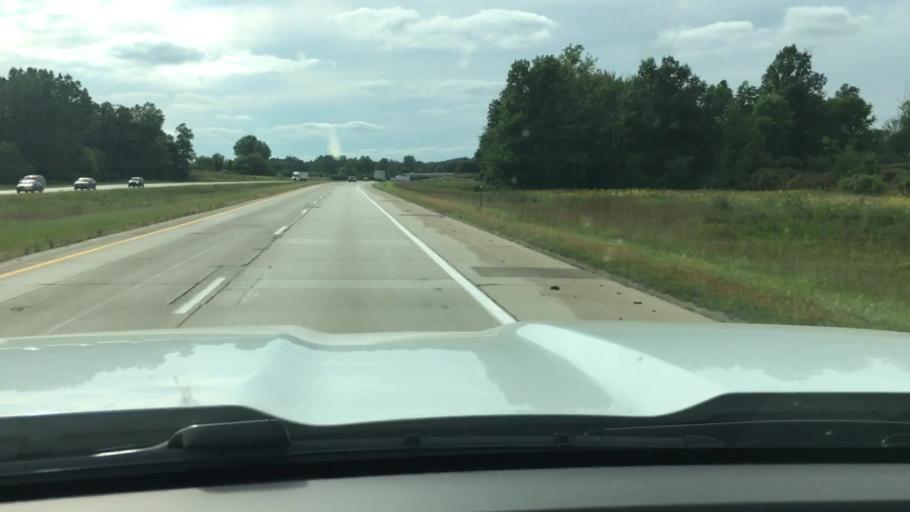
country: US
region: Michigan
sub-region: Lapeer County
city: Lapeer
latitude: 43.0119
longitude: -83.2731
